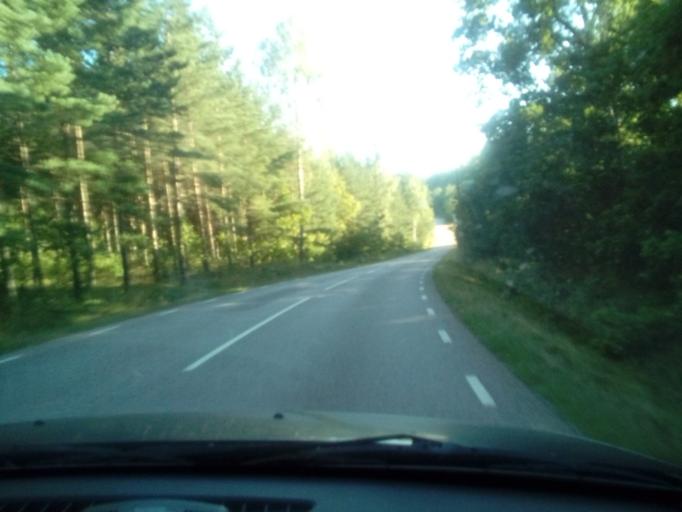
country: SE
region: Kalmar
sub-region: Vasterviks Kommun
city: Gamleby
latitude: 57.8155
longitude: 16.4402
